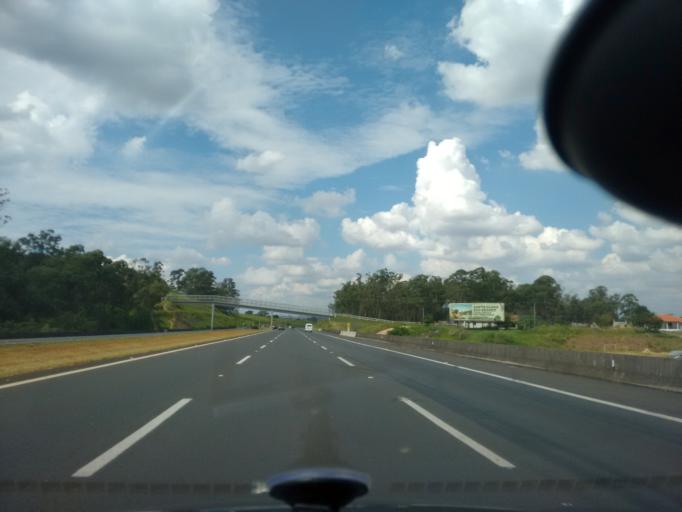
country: BR
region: Sao Paulo
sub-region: Hortolandia
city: Hortolandia
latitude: -22.9115
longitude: -47.1751
